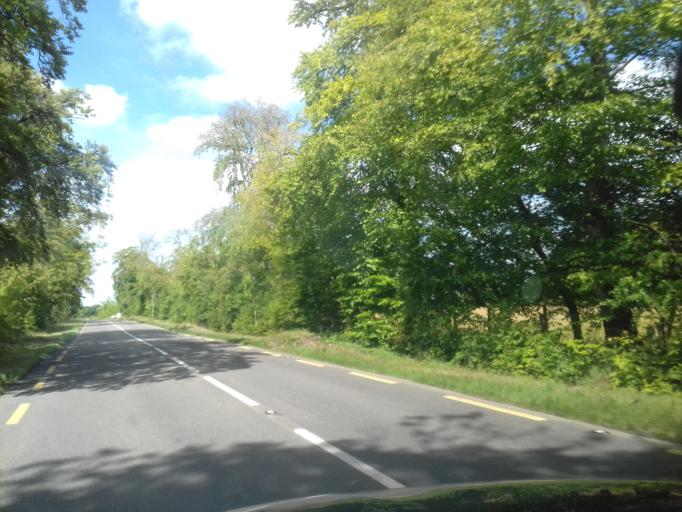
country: IE
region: Leinster
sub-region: Wicklow
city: Blessington
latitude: 53.1434
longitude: -6.5593
